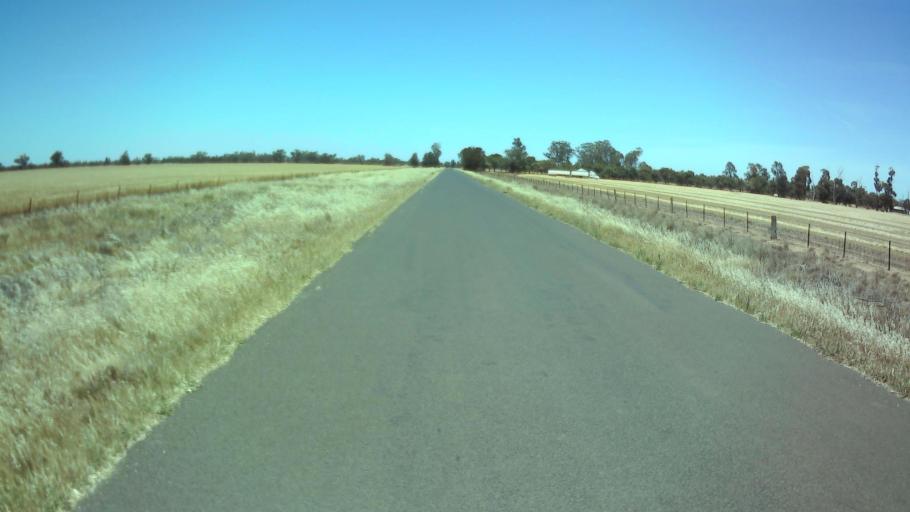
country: AU
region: New South Wales
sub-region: Weddin
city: Grenfell
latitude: -34.0275
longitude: 147.7913
